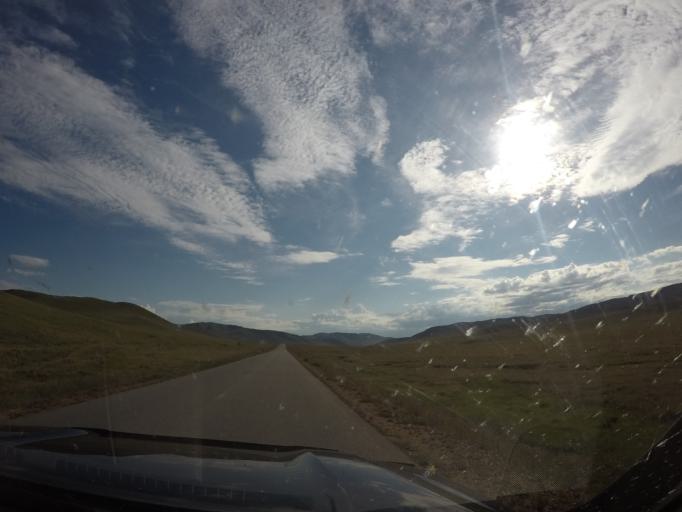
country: MN
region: Hentiy
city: Modot
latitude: 47.7240
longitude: 108.5846
